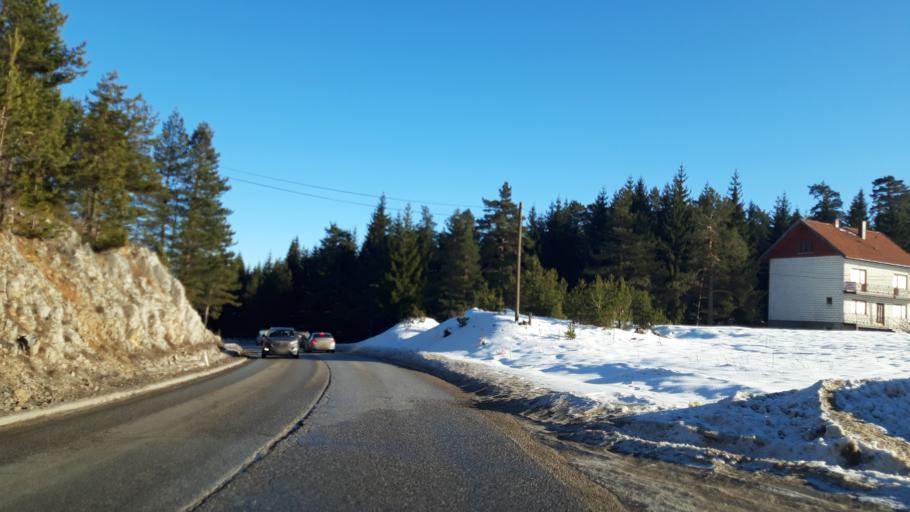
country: BA
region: Republika Srpska
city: Sokolac
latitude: 43.9077
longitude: 18.7087
